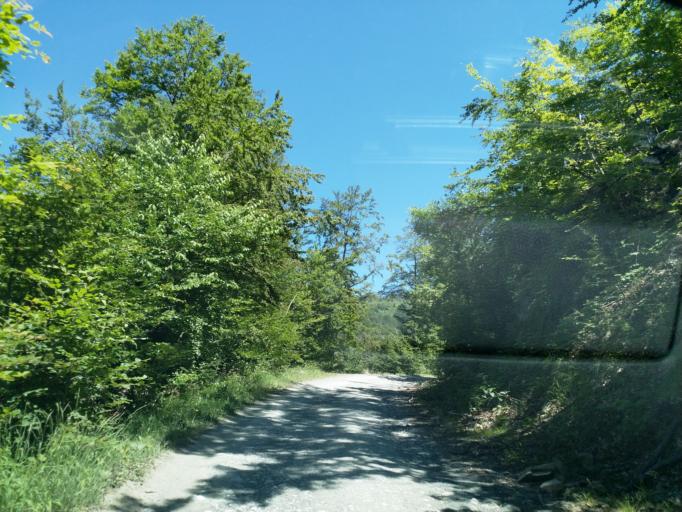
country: XK
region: Mitrovica
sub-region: Komuna e Leposaviqit
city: Leposaviq
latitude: 43.2748
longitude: 20.8725
